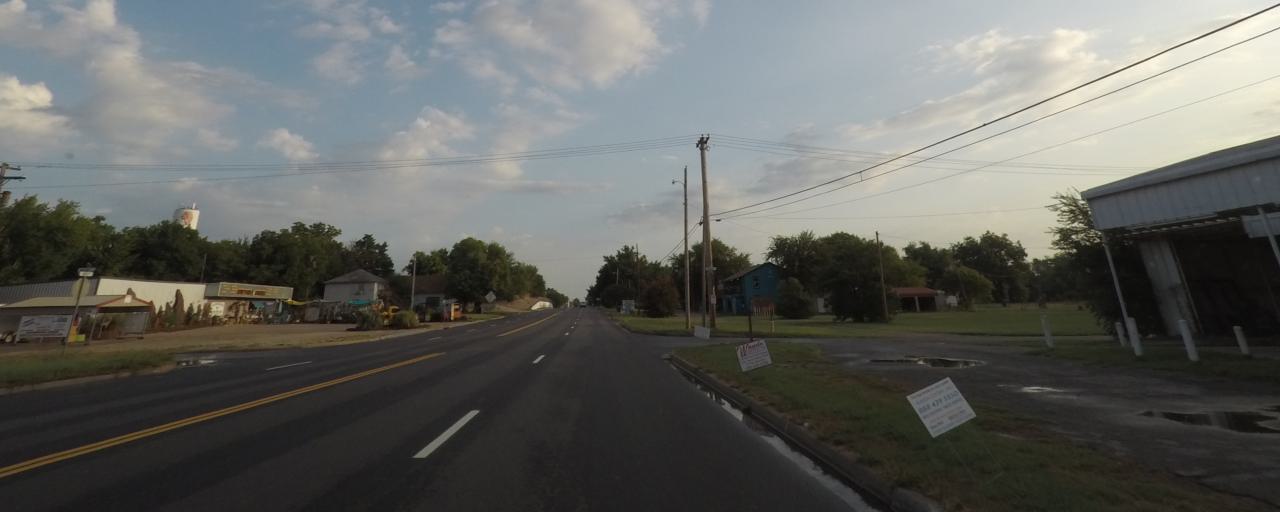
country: US
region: Oklahoma
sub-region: Stephens County
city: Comanche
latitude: 34.3623
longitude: -97.9642
